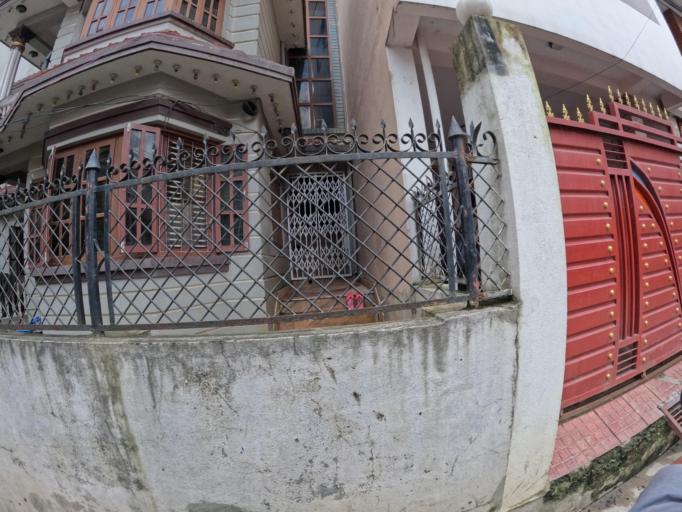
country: NP
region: Central Region
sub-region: Bagmati Zone
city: Kathmandu
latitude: 27.7453
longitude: 85.3176
